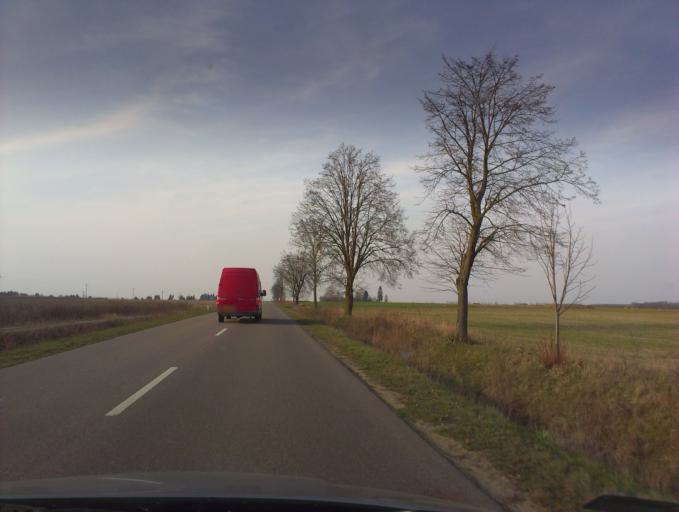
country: PL
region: Pomeranian Voivodeship
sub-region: Powiat czluchowski
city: Debrzno
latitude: 53.5492
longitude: 17.2317
